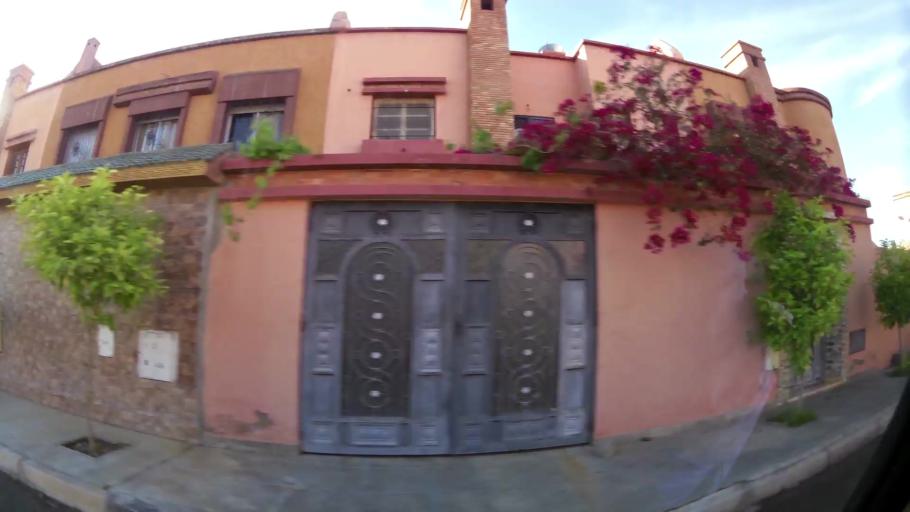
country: MA
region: Marrakech-Tensift-Al Haouz
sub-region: Marrakech
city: Marrakesh
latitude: 31.7575
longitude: -8.1054
